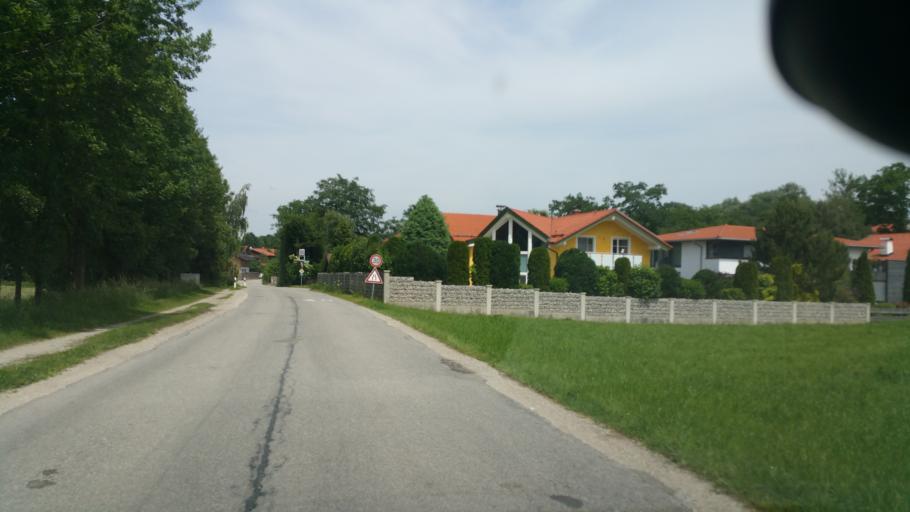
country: DE
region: Bavaria
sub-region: Upper Bavaria
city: Aschau im Chiemgau
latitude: 47.7900
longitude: 12.3259
